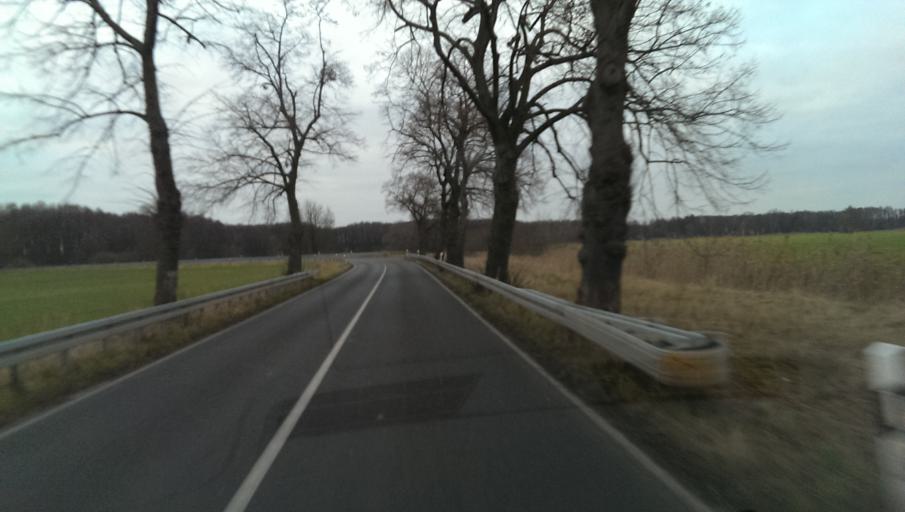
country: DE
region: Brandenburg
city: Am Mellensee
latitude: 52.1609
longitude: 13.4253
